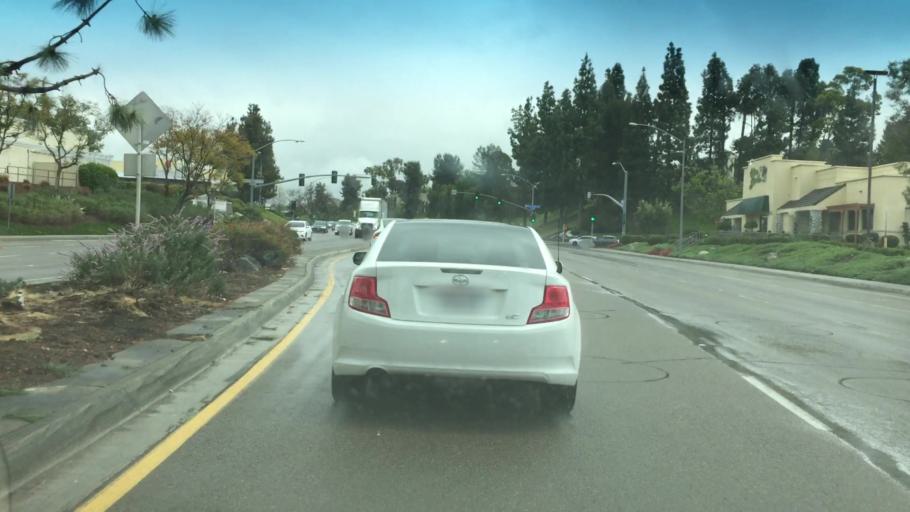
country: US
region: California
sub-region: San Diego County
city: Poway
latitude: 32.9788
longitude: -117.0833
